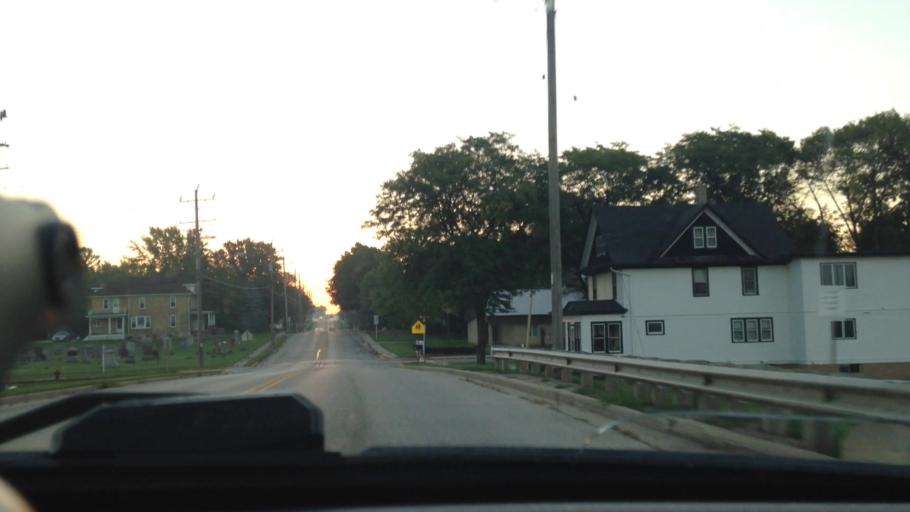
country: US
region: Wisconsin
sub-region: Dodge County
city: Lomira
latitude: 43.5871
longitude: -88.4411
